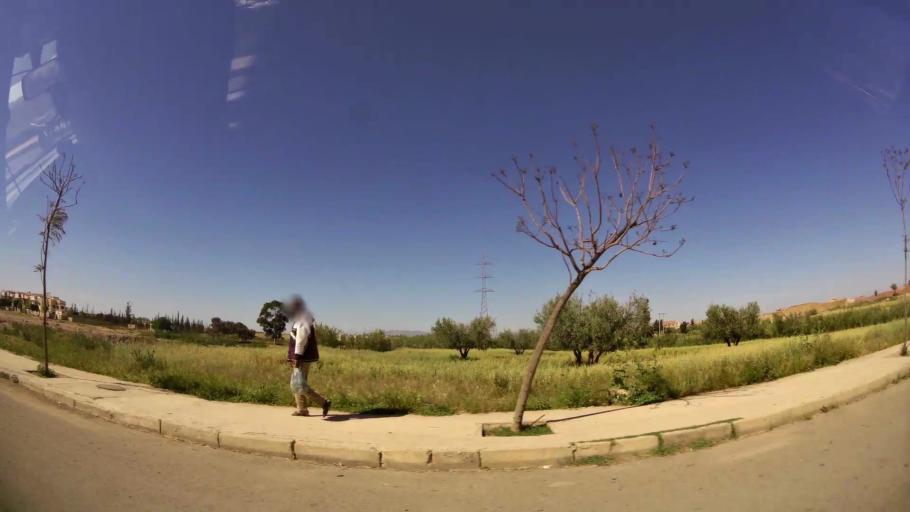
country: MA
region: Oriental
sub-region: Oujda-Angad
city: Oujda
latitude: 34.7218
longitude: -1.9066
